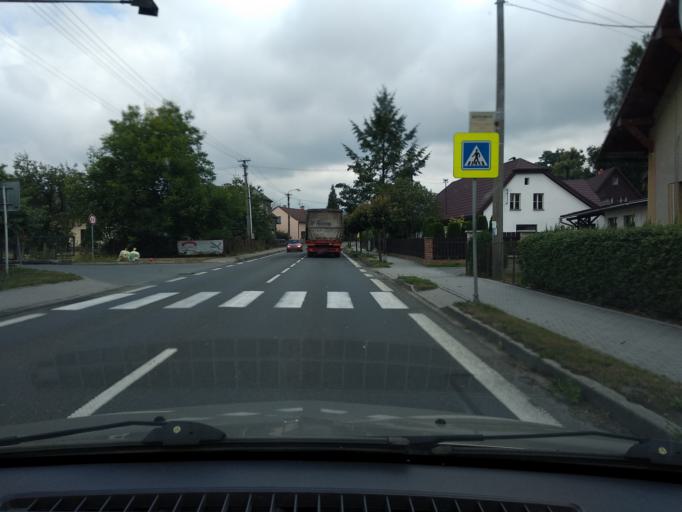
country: CZ
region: Olomoucky
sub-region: Okres Sumperk
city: Bludov
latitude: 49.9376
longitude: 16.9287
